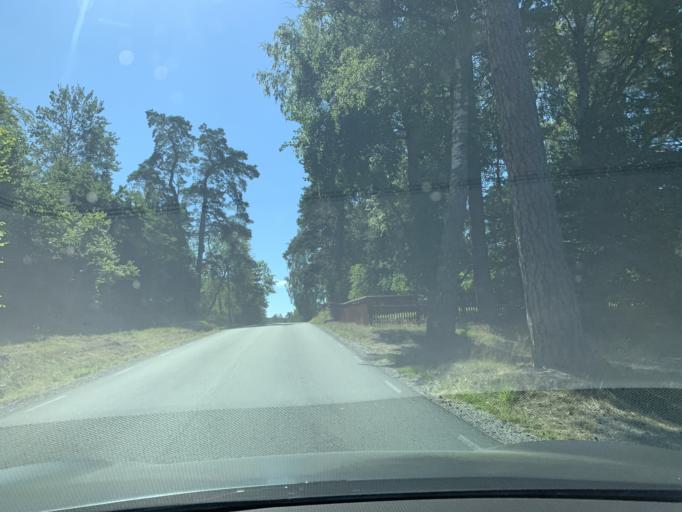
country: SE
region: Stockholm
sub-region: Botkyrka Kommun
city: Eriksberg
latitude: 59.2441
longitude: 17.7868
